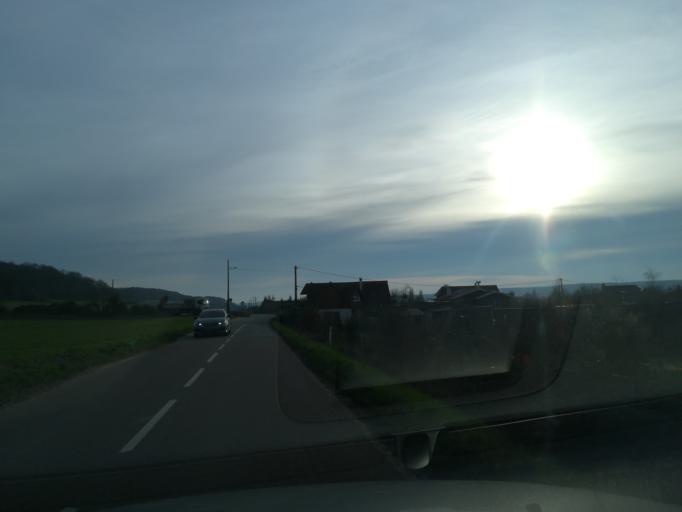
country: FR
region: Haute-Normandie
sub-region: Departement de la Seine-Maritime
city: Saint-Martin-de-Boscherville
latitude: 49.4285
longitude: 0.9576
